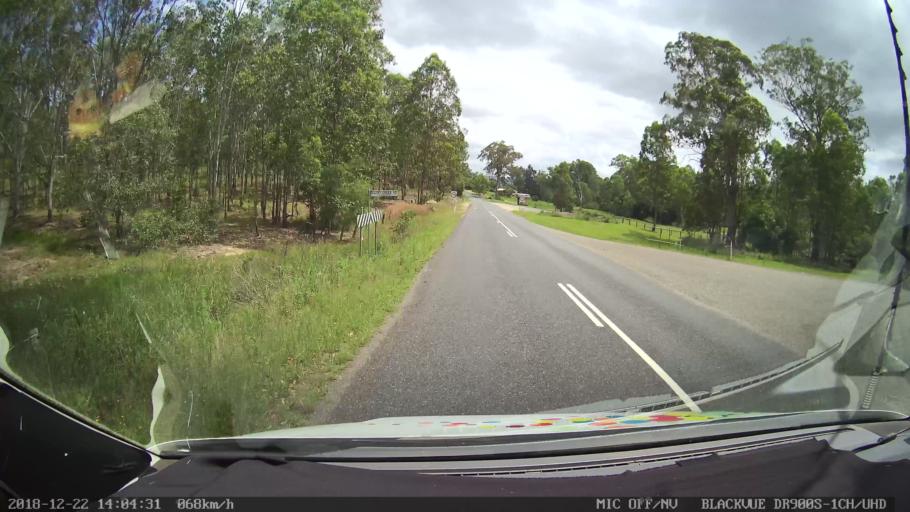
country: AU
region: New South Wales
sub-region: Clarence Valley
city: Coutts Crossing
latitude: -29.9352
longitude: 152.7289
